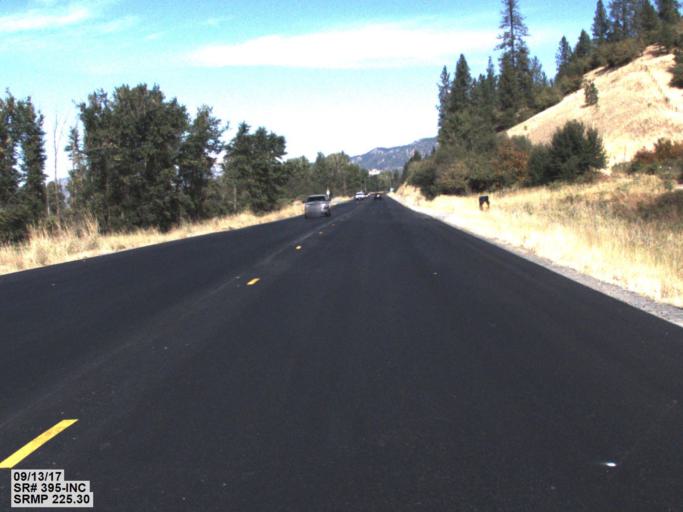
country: US
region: Washington
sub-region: Stevens County
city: Colville
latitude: 48.4845
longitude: -117.9023
